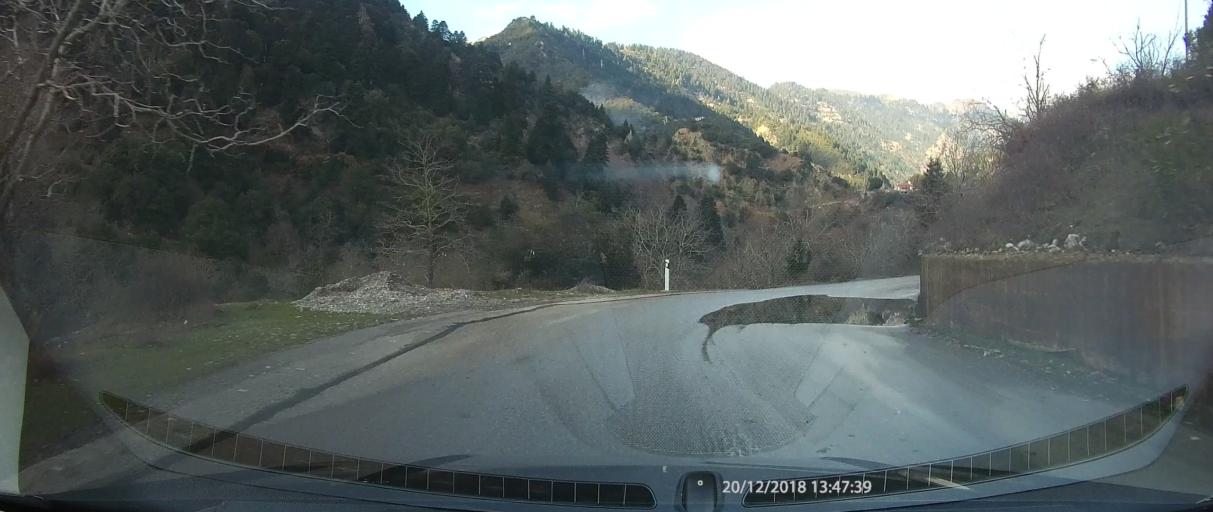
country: GR
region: West Greece
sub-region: Nomos Aitolias kai Akarnanias
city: Thermo
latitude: 38.6830
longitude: 21.6128
